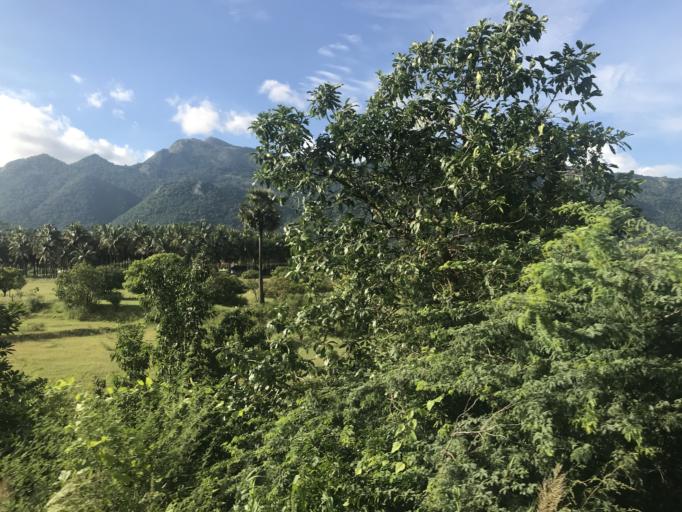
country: IN
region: Tamil Nadu
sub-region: Coimbatore
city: Madukkarai
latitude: 10.8778
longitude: 76.8632
